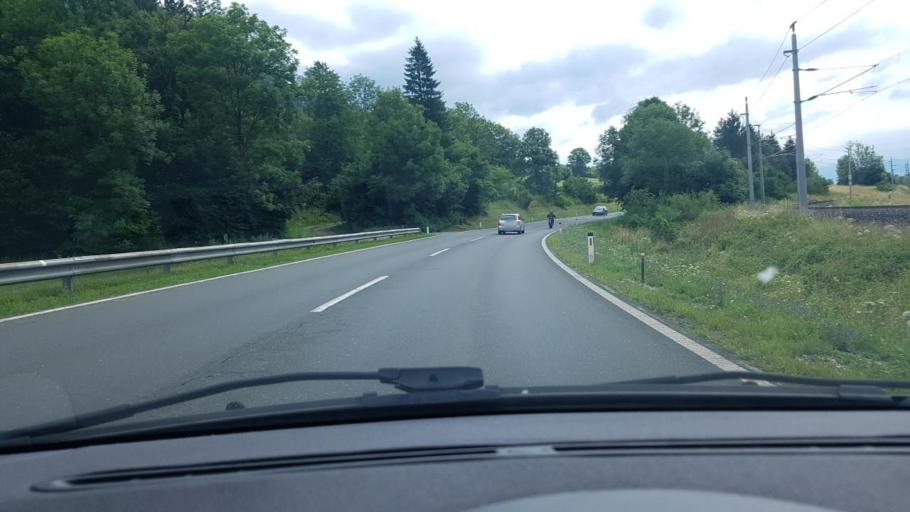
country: AT
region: Carinthia
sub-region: Politischer Bezirk Hermagor
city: Hermagor
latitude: 46.6330
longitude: 13.4019
